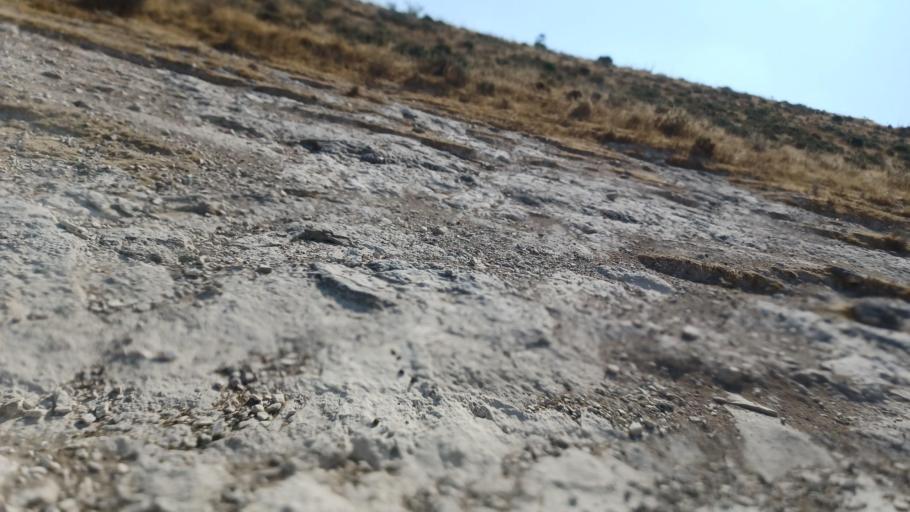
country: CY
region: Lefkosia
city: Lympia
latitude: 34.9838
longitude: 33.4791
